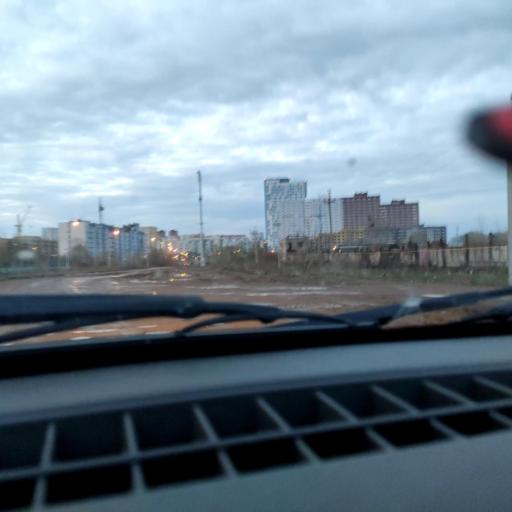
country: RU
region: Bashkortostan
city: Ufa
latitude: 54.6797
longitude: 55.9788
